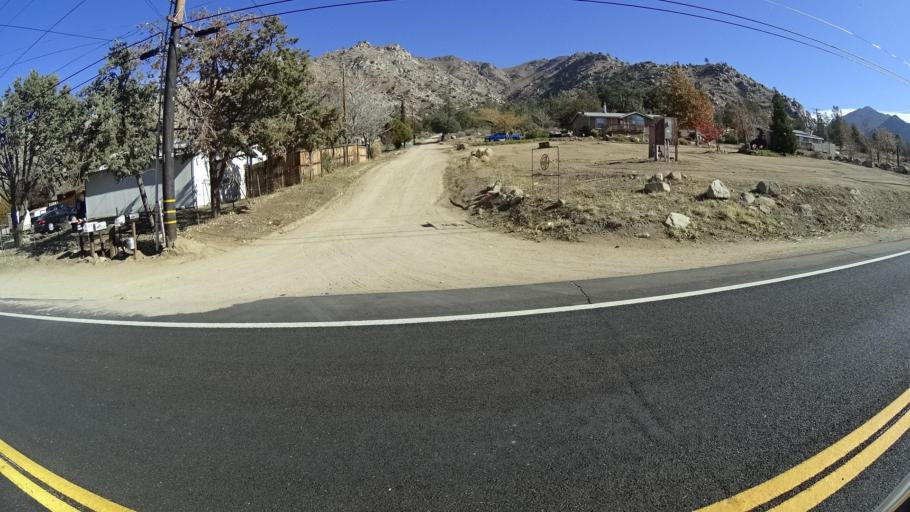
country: US
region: California
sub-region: Kern County
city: Lake Isabella
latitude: 35.6156
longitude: -118.4684
